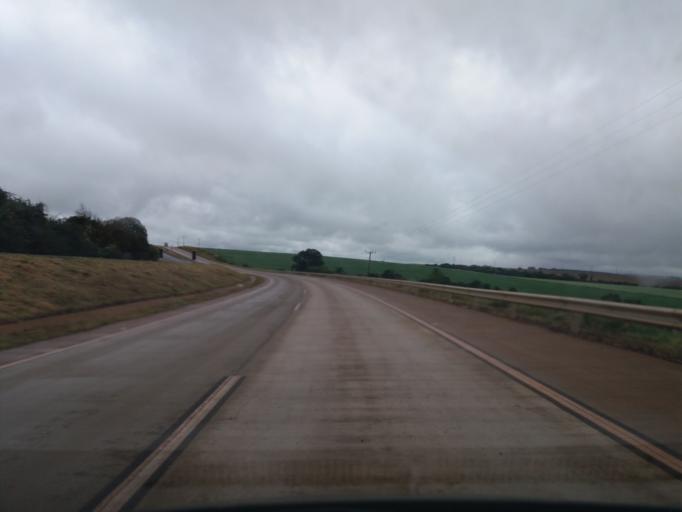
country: BR
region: Parana
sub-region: Cascavel
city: Cascavel
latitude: -25.0469
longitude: -53.5564
